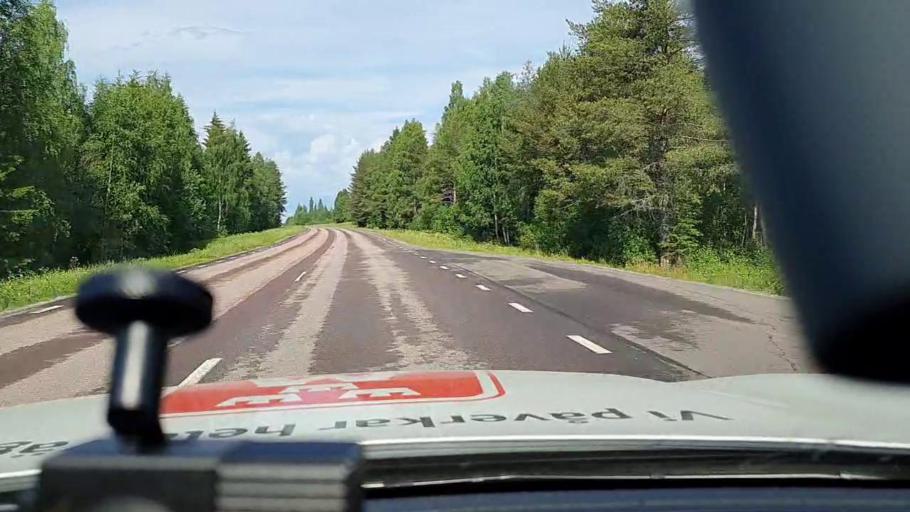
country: SE
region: Norrbotten
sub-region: Alvsbyns Kommun
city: AElvsbyn
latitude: 66.0217
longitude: 21.1319
